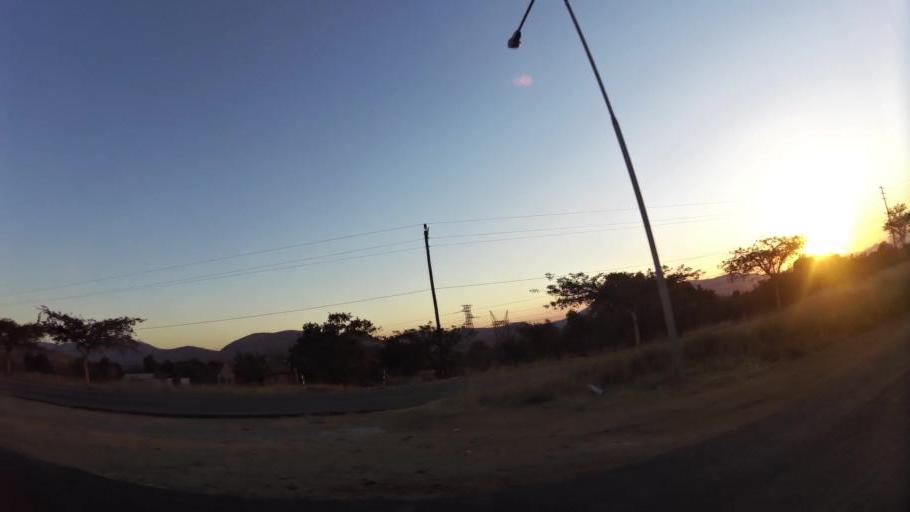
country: ZA
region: North-West
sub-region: Bojanala Platinum District Municipality
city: Rustenburg
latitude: -25.6135
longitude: 27.1782
